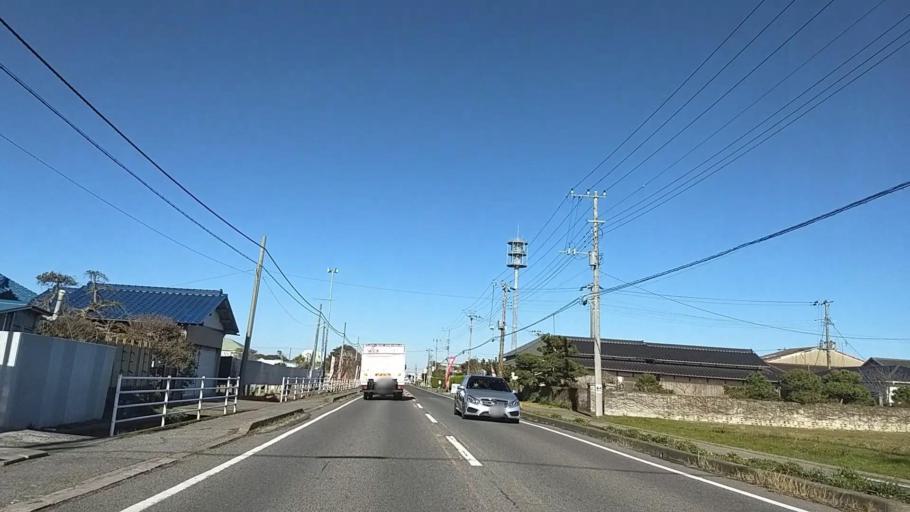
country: JP
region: Chiba
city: Togane
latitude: 35.4933
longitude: 140.4246
